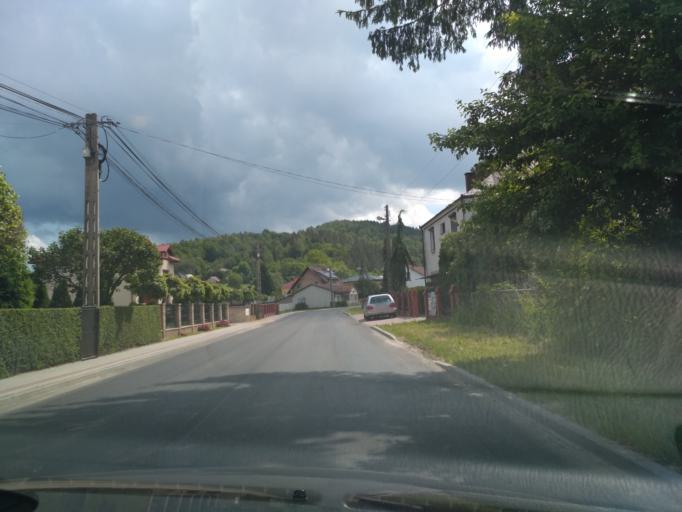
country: PL
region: Subcarpathian Voivodeship
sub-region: Powiat rzeszowski
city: Blazowa
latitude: 49.8802
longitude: 22.0932
